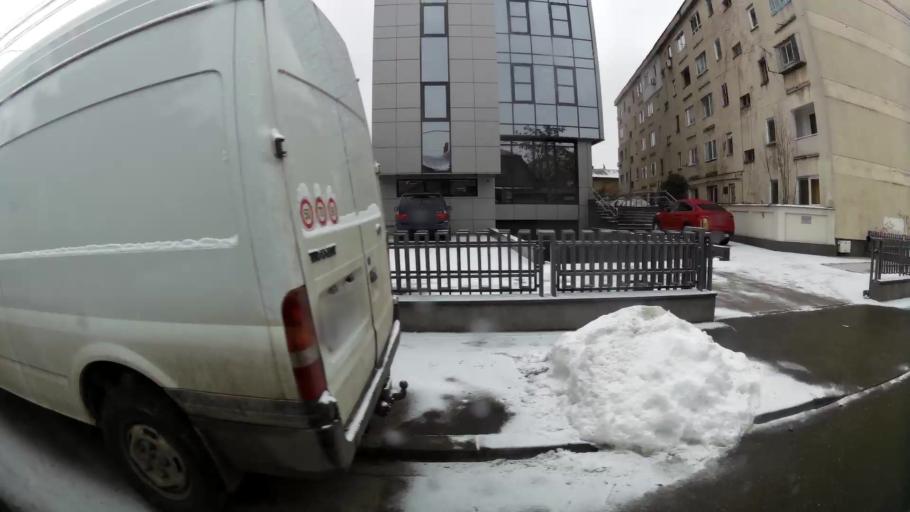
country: RO
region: Prahova
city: Ploiesti
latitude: 44.9480
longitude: 26.0154
